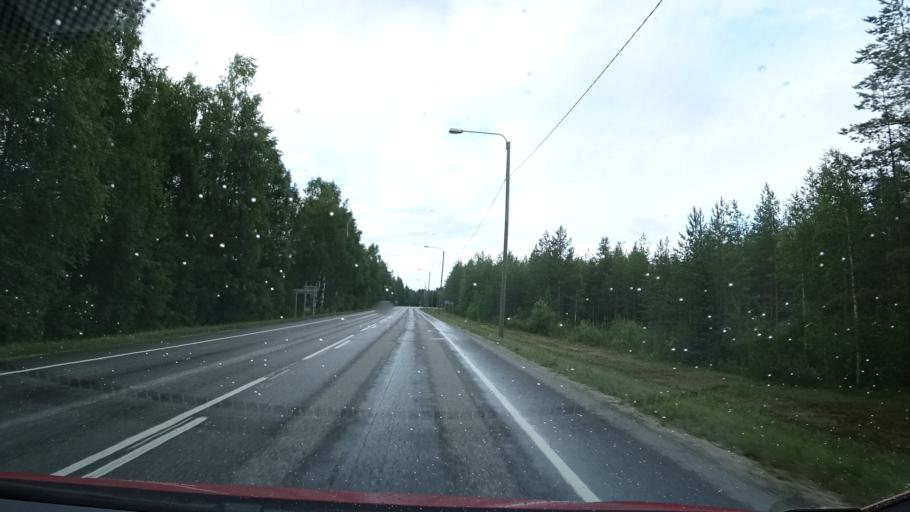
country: FI
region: Kainuu
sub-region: Kehys-Kainuu
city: Kuhmo
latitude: 64.1124
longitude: 29.4910
